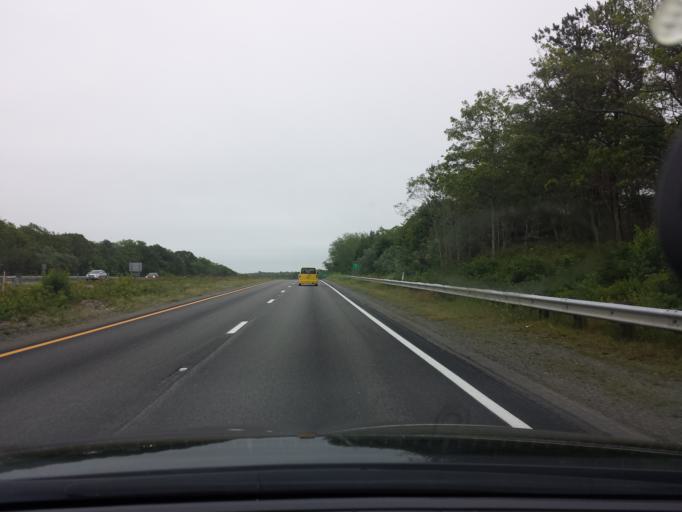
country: US
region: Massachusetts
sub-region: Barnstable County
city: East Sandwich
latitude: 41.7330
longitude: -70.4632
